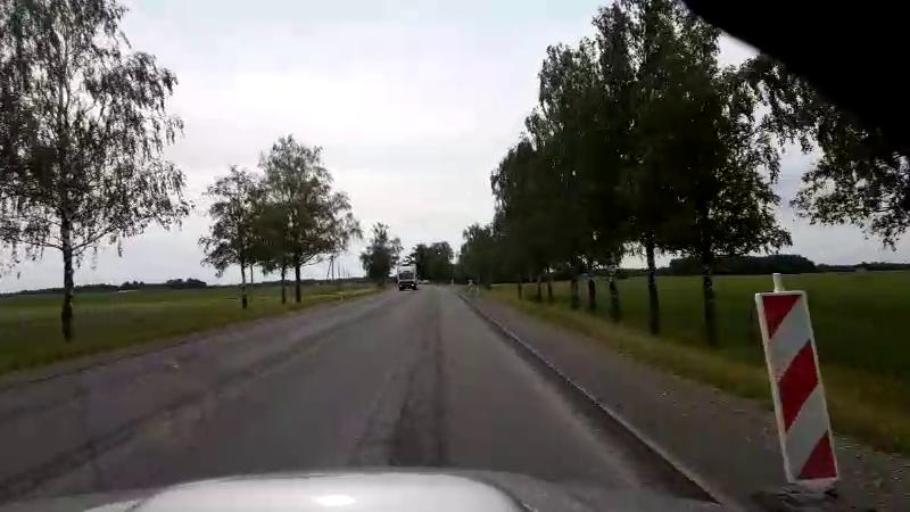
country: LV
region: Bauskas Rajons
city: Bauska
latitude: 56.3414
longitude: 24.2923
